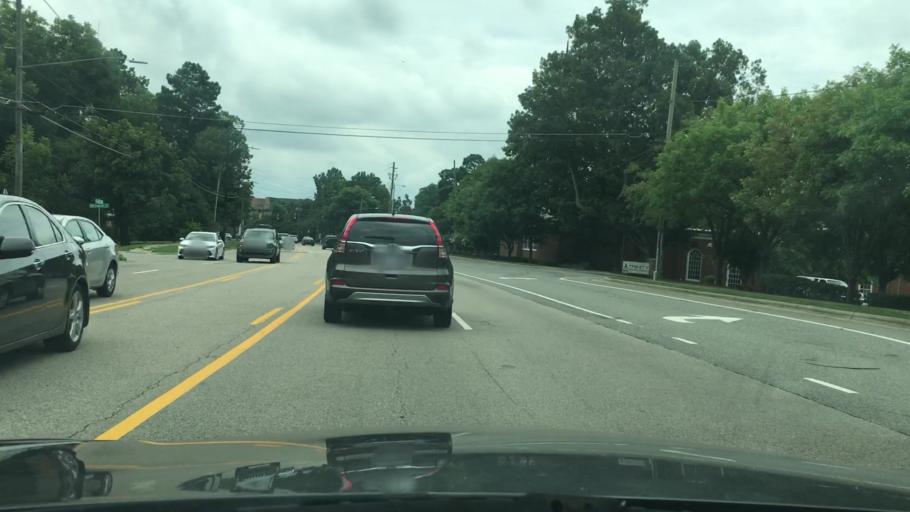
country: US
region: North Carolina
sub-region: Wake County
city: West Raleigh
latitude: 35.8478
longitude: -78.6443
